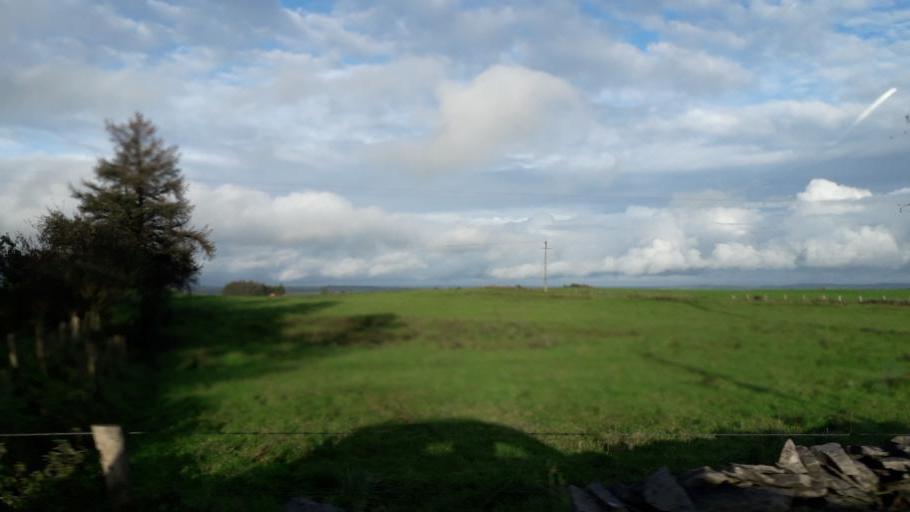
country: IE
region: Connaught
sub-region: Roscommon
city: Boyle
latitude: 53.8042
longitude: -8.3024
